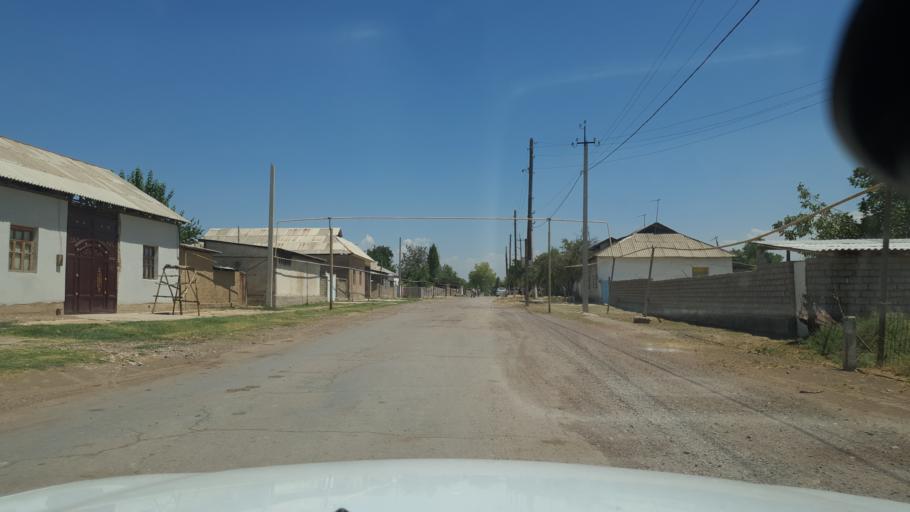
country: UZ
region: Toshkent
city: Piskent
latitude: 40.8261
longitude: 69.4030
